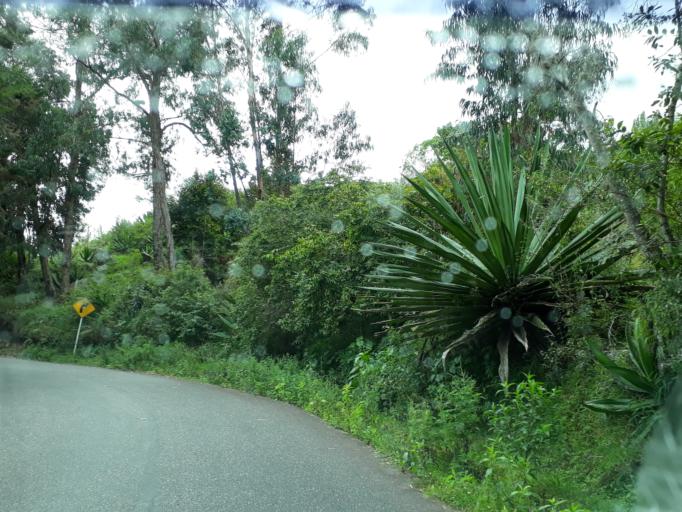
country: CO
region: Cundinamarca
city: Cabrera
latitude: 4.0145
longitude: -74.5090
